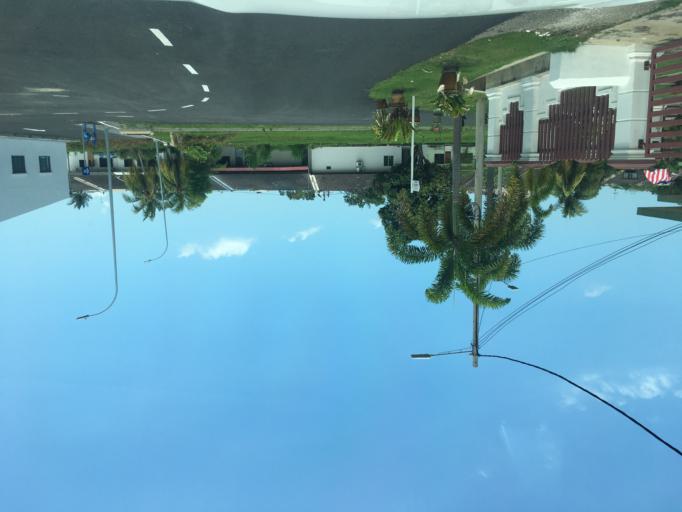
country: MY
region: Melaka
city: Kampung Ayer Molek
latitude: 2.2025
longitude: 102.3089
